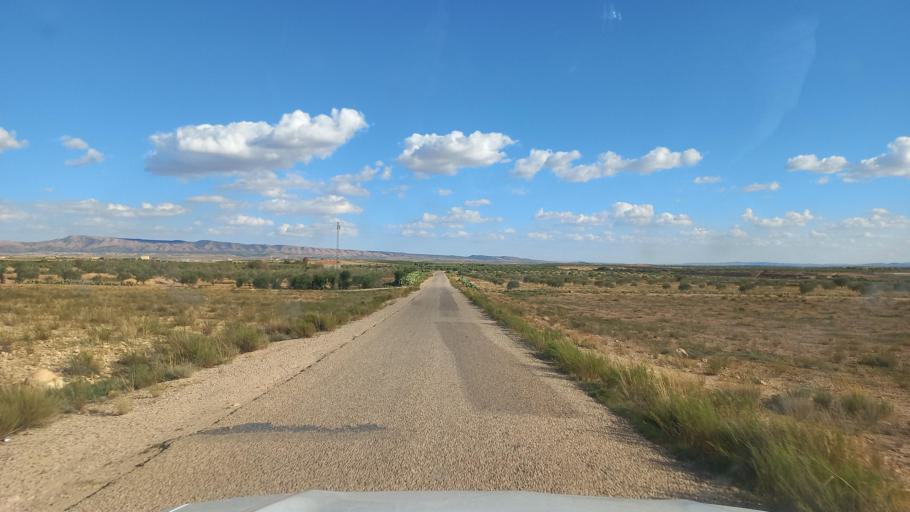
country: TN
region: Al Qasrayn
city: Sbiba
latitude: 35.3890
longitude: 9.0278
